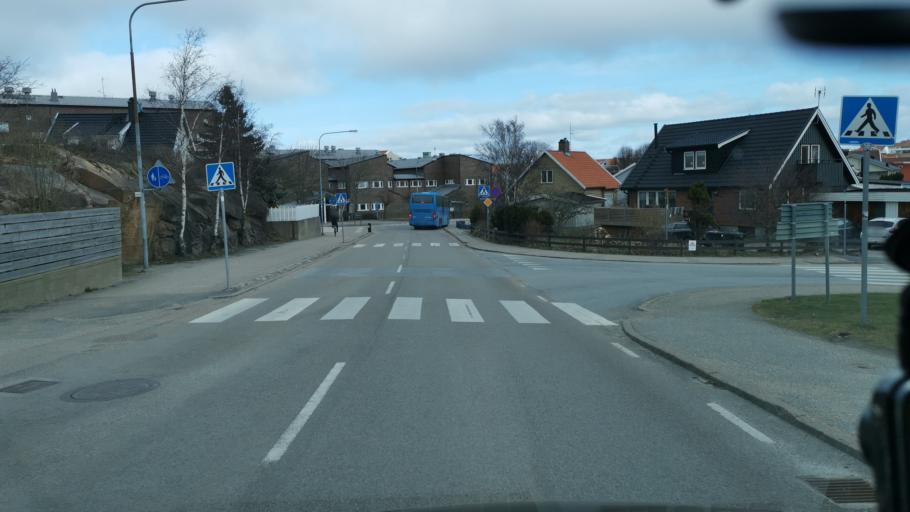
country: SE
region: Vaestra Goetaland
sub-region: Lysekils Kommun
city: Lysekil
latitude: 58.2796
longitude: 11.4388
